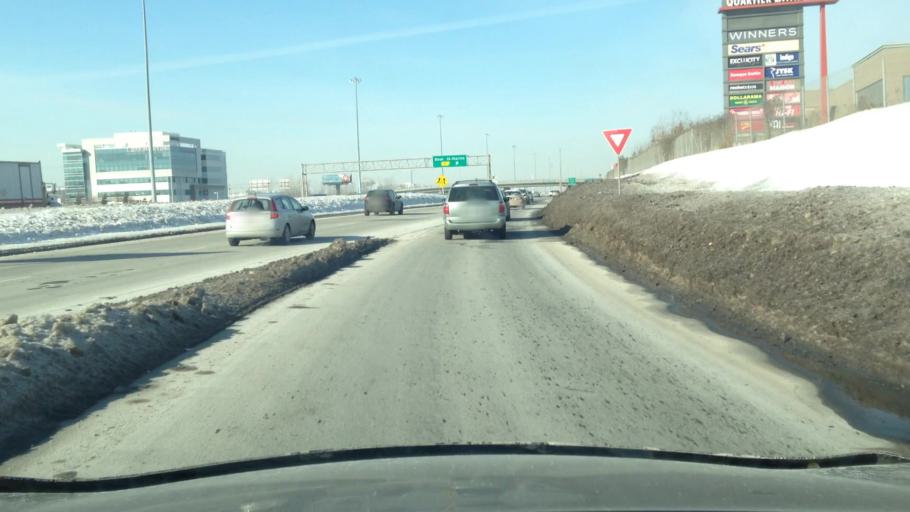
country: CA
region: Quebec
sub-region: Laval
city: Laval
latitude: 45.5545
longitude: -73.7273
